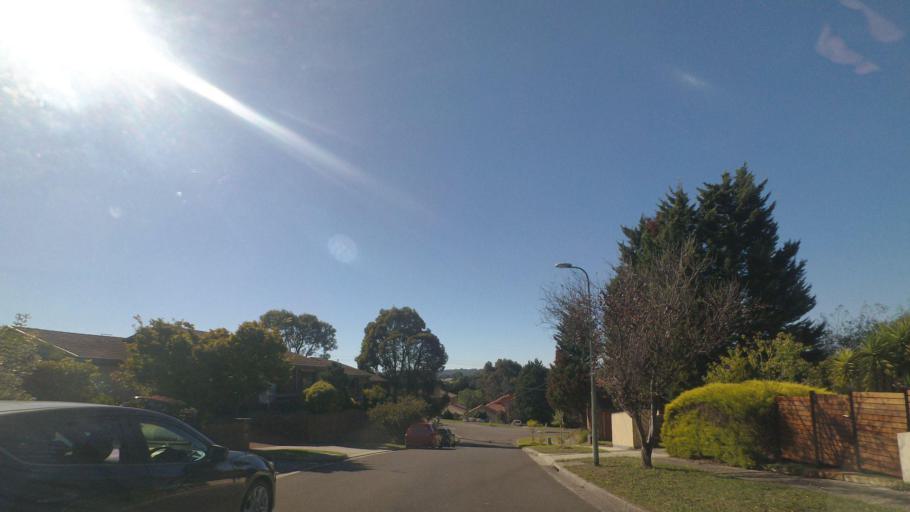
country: AU
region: Victoria
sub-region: Manningham
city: Donvale
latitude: -37.7778
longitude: 145.1770
